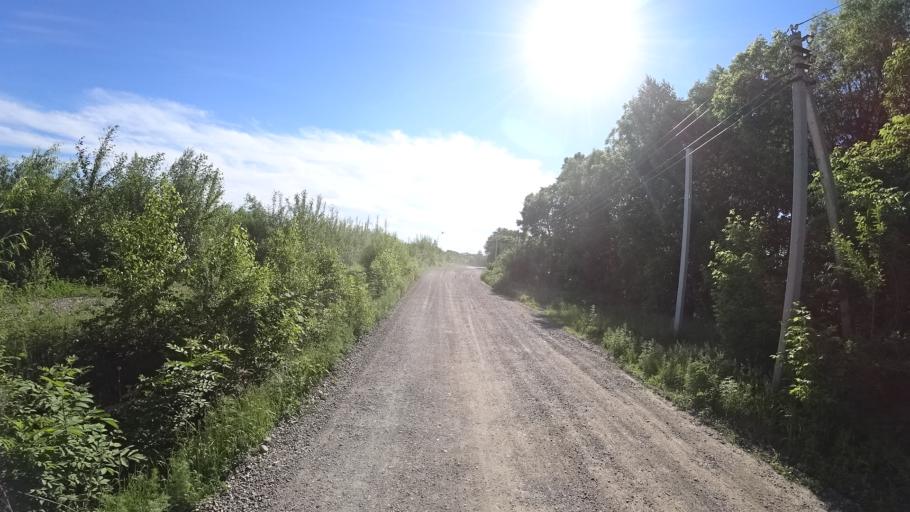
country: RU
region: Khabarovsk Krai
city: Khor
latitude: 47.8859
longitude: 135.0006
